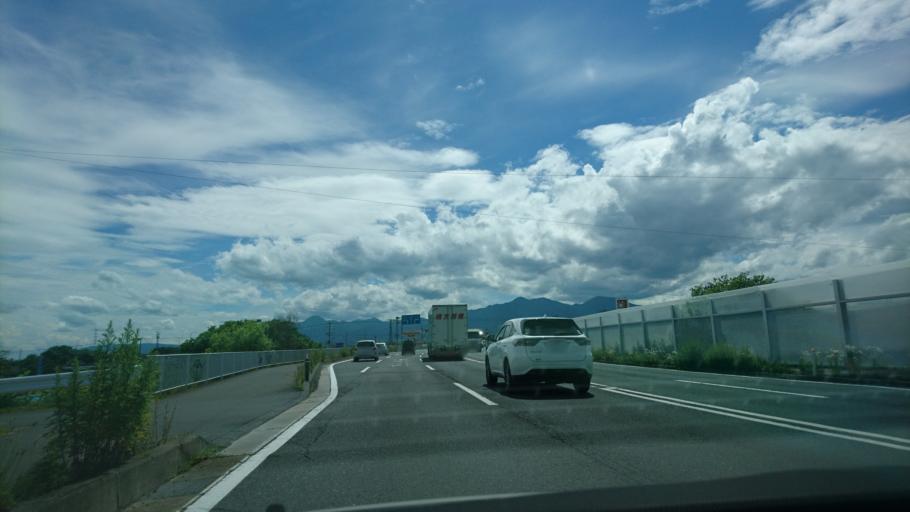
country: JP
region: Iwate
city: Morioka-shi
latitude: 39.6864
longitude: 141.1633
